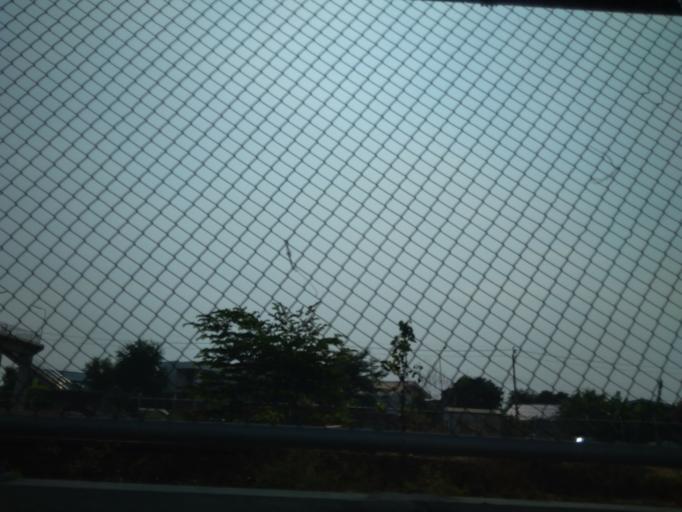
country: TH
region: Bangkok
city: Taling Chan
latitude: 13.7873
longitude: 100.4429
